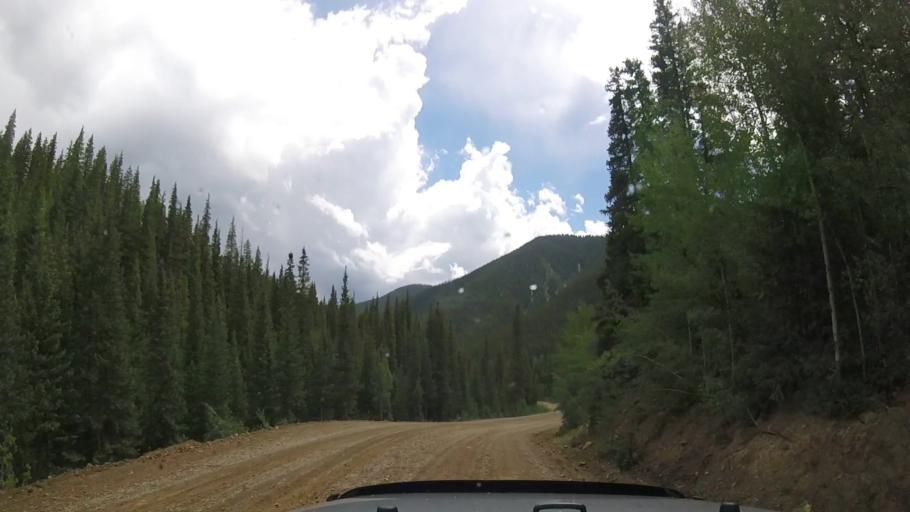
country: US
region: Colorado
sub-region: San Juan County
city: Silverton
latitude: 37.8445
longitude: -107.6790
